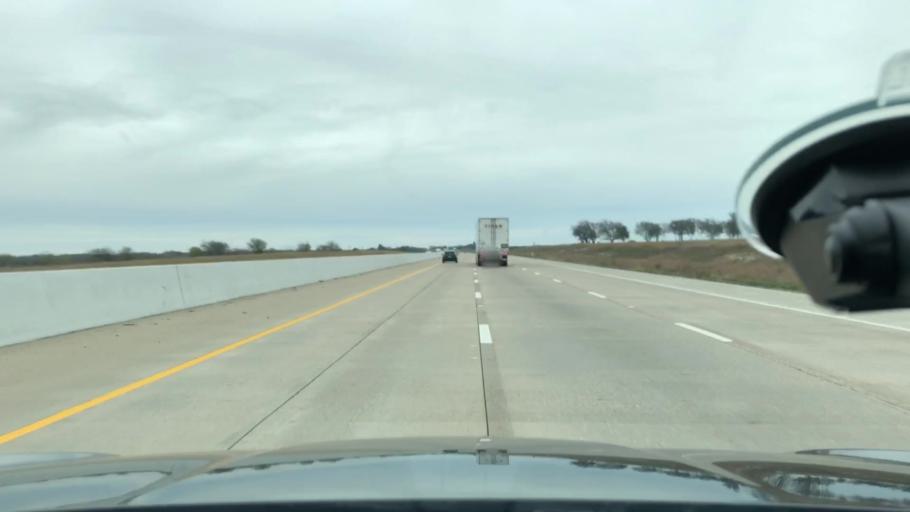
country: US
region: Texas
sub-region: Ellis County
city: Italy
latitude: 32.1636
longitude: -96.9201
